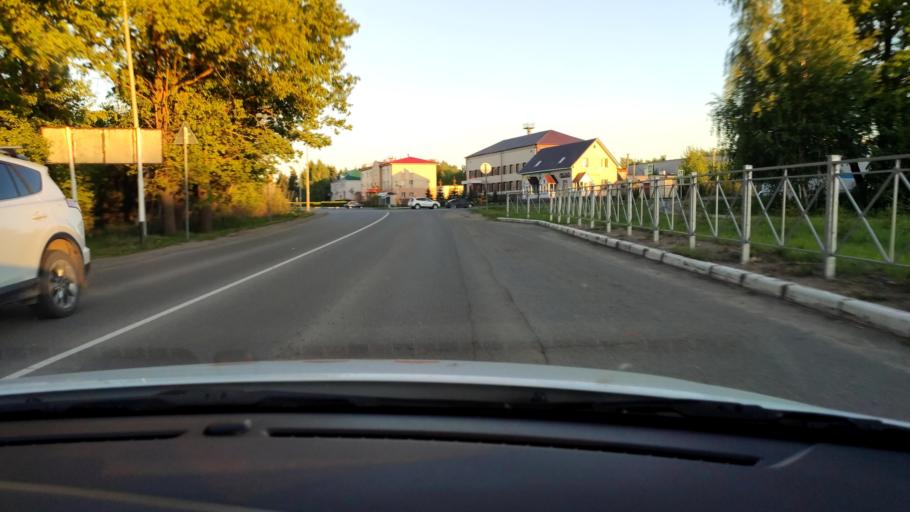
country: RU
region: Tatarstan
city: Vysokaya Gora
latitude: 55.9227
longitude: 49.3057
